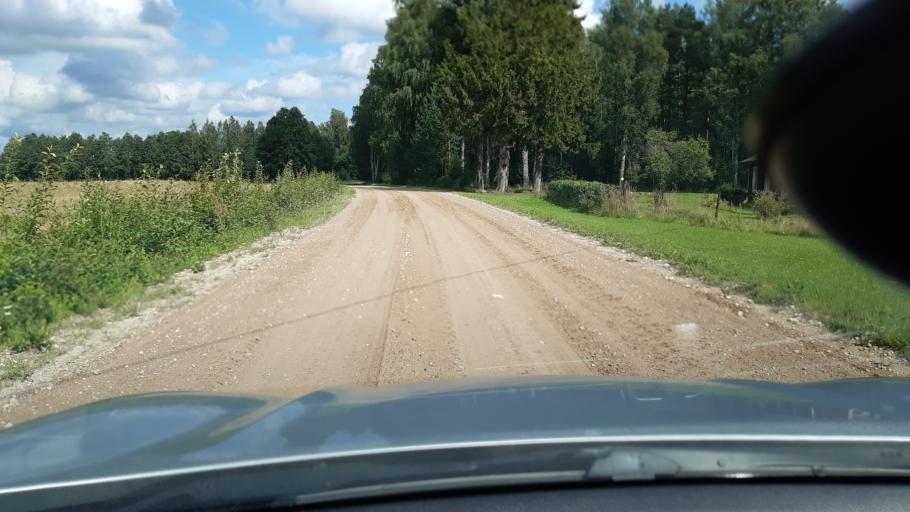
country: EE
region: Jaervamaa
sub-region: Tueri vald
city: Tueri
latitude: 58.9367
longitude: 25.2476
